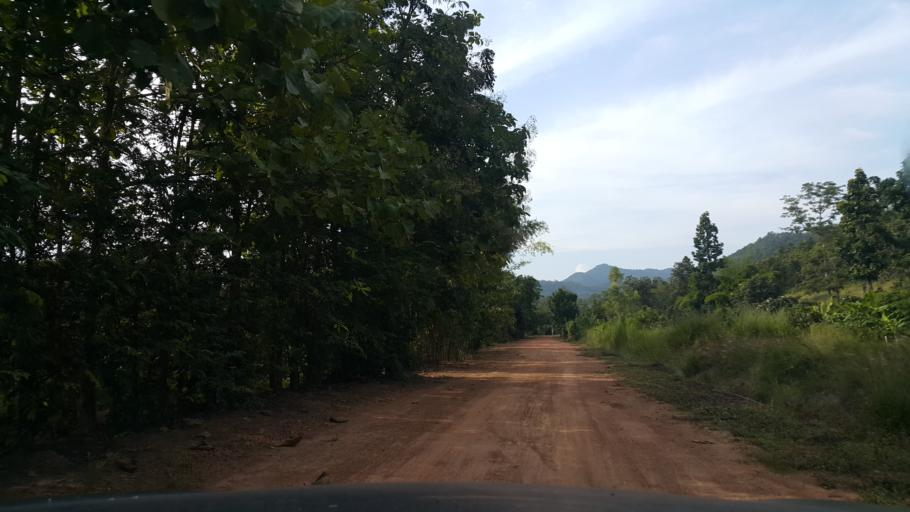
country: TH
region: Chiang Mai
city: San Sai
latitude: 18.9136
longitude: 99.1026
